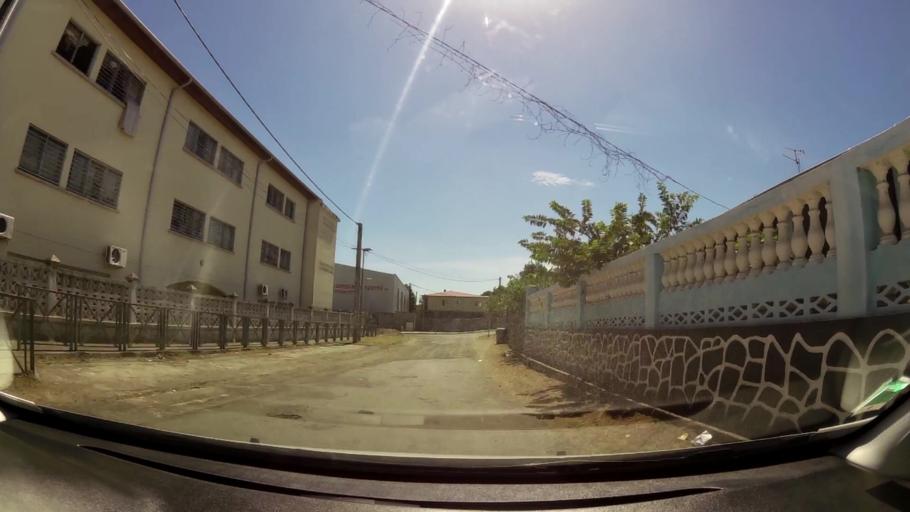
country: YT
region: Pamandzi
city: Pamandzi
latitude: -12.7968
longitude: 45.2812
